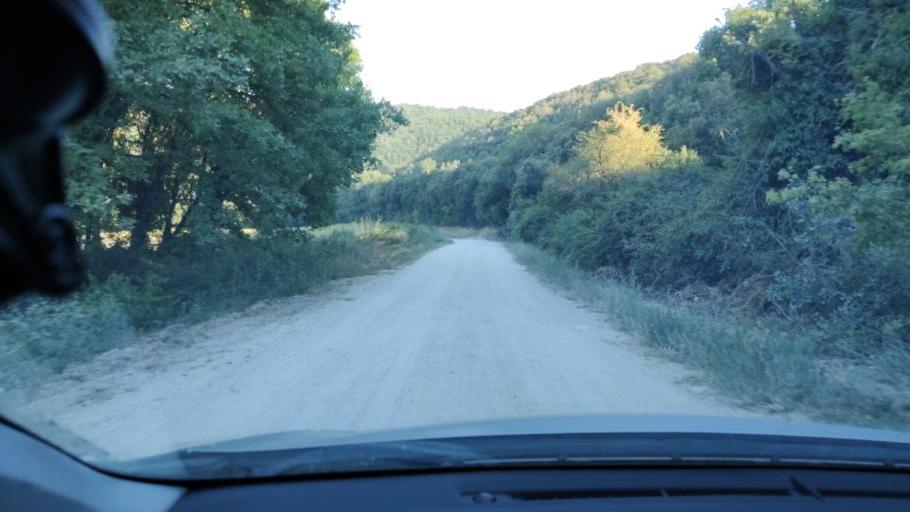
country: IT
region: Umbria
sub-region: Provincia di Terni
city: Amelia
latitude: 42.5419
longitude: 12.3838
